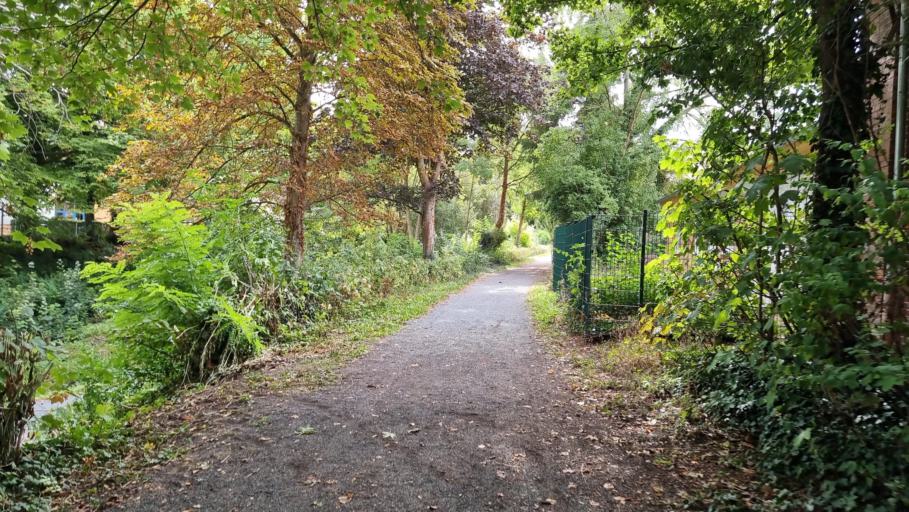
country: DE
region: Lower Saxony
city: Alfeld
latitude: 51.9887
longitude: 9.8267
